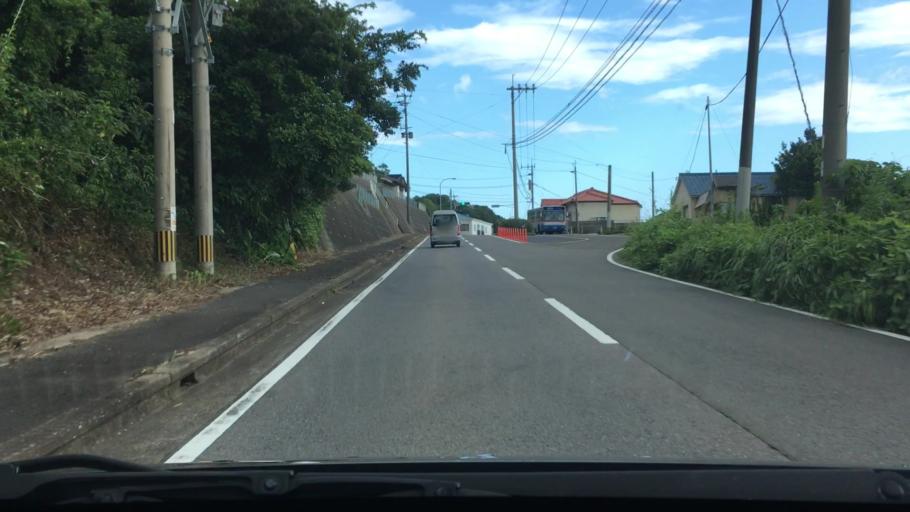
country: JP
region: Nagasaki
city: Togitsu
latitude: 32.8641
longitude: 129.6835
